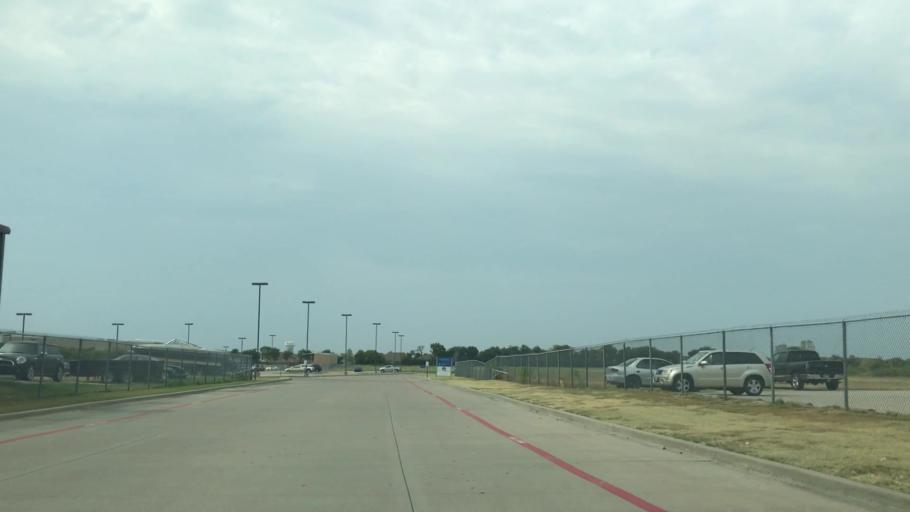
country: US
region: Texas
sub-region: Tarrant County
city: Keller
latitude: 32.9099
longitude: -97.2602
